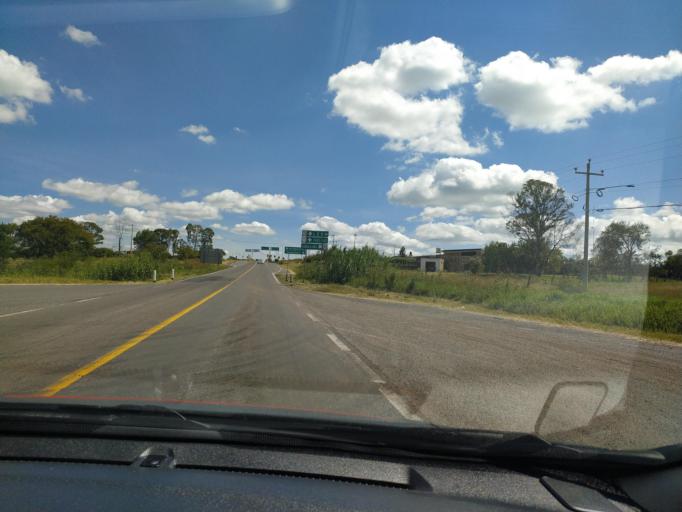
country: MX
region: Jalisco
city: Valle de Guadalupe
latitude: 21.0332
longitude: -102.5557
